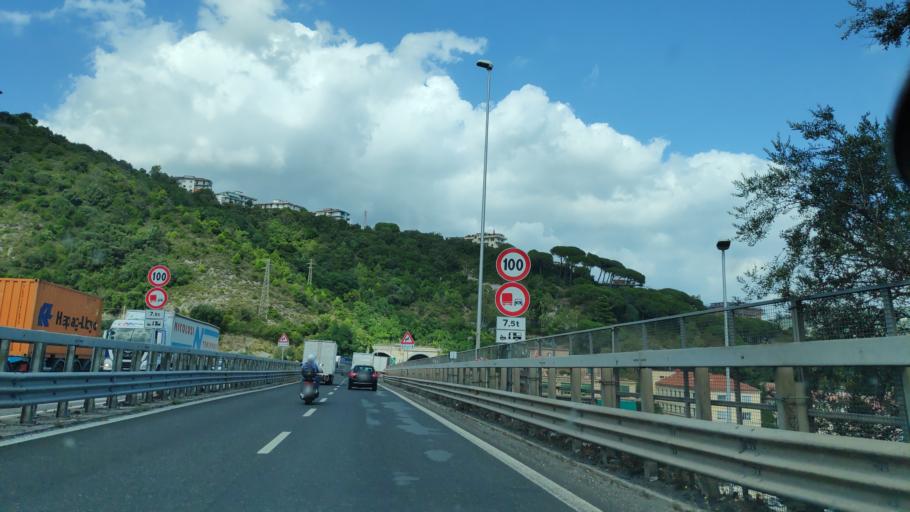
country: IT
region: Campania
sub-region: Provincia di Salerno
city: Capezzano Inferiore
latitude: 40.6854
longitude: 14.7617
